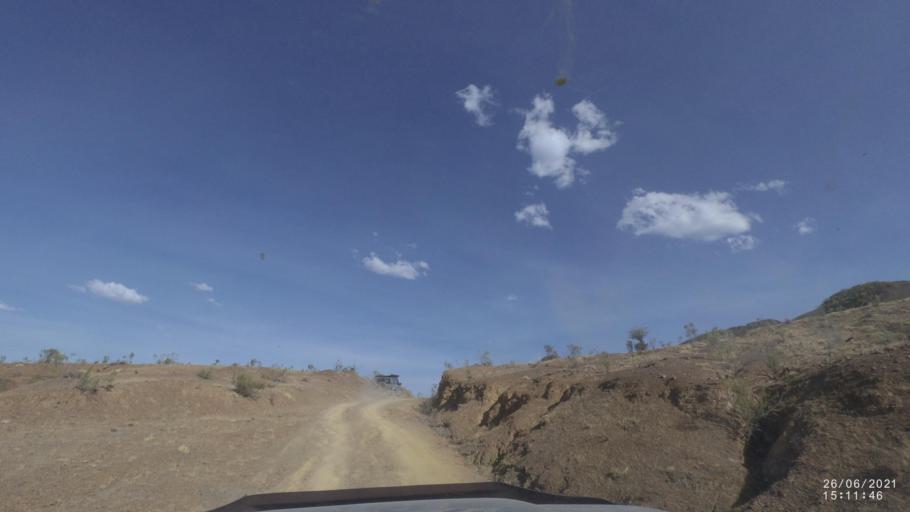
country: BO
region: Cochabamba
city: Mizque
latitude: -17.9568
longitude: -65.6431
